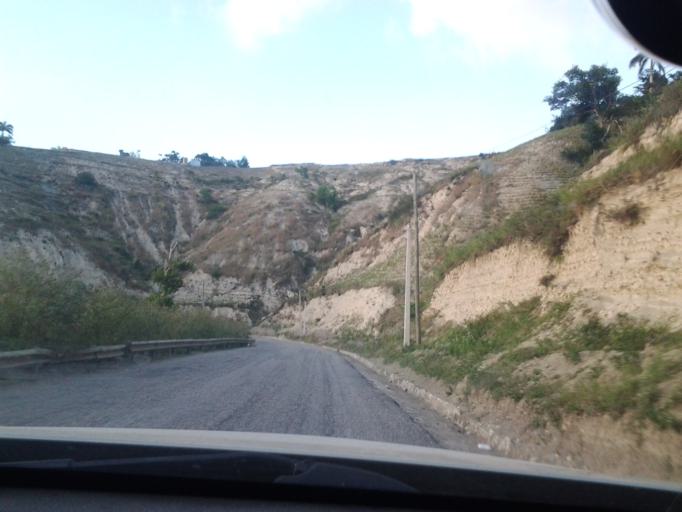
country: HT
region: Sud-Est
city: Jacmel
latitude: 18.3631
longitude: -72.5860
